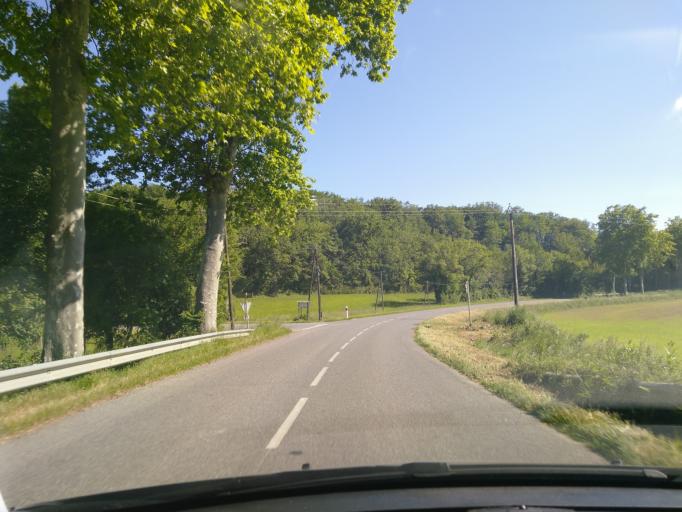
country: FR
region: Midi-Pyrenees
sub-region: Departement du Gers
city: Aubiet
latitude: 43.5317
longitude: 0.7653
